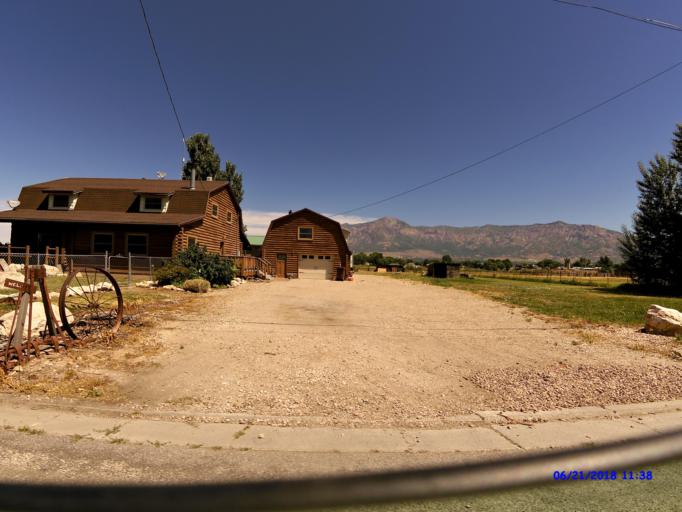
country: US
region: Utah
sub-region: Weber County
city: Harrisville
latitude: 41.2668
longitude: -111.9847
